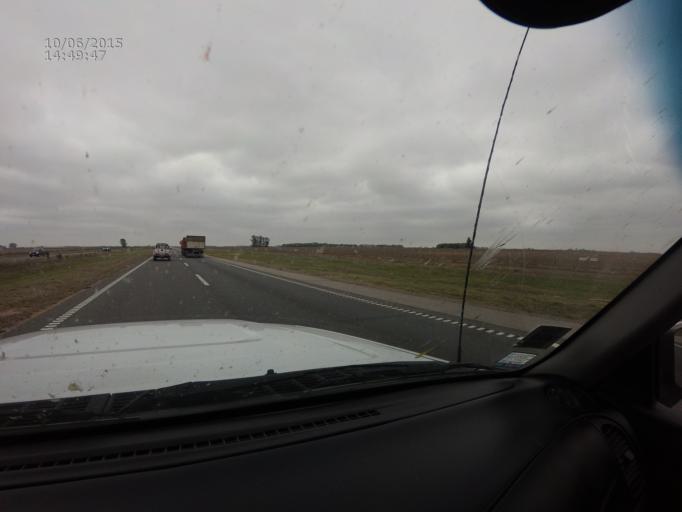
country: AR
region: Cordoba
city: Oncativo
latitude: -31.9231
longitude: -63.6226
